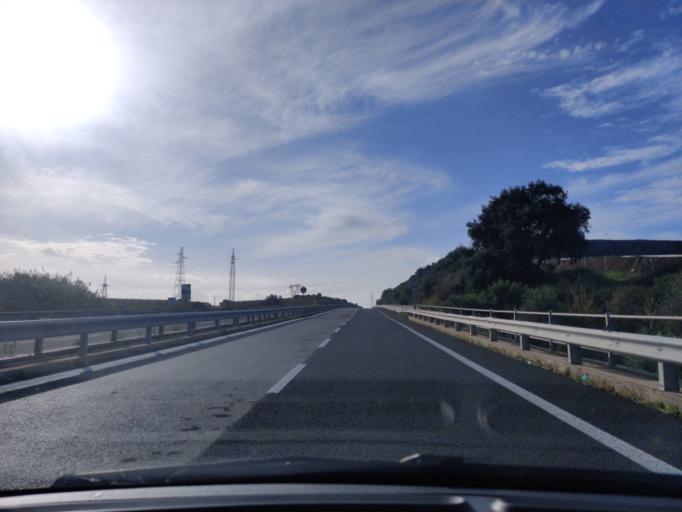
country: IT
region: Latium
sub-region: Citta metropolitana di Roma Capitale
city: Aurelia
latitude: 42.1174
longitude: 11.7916
